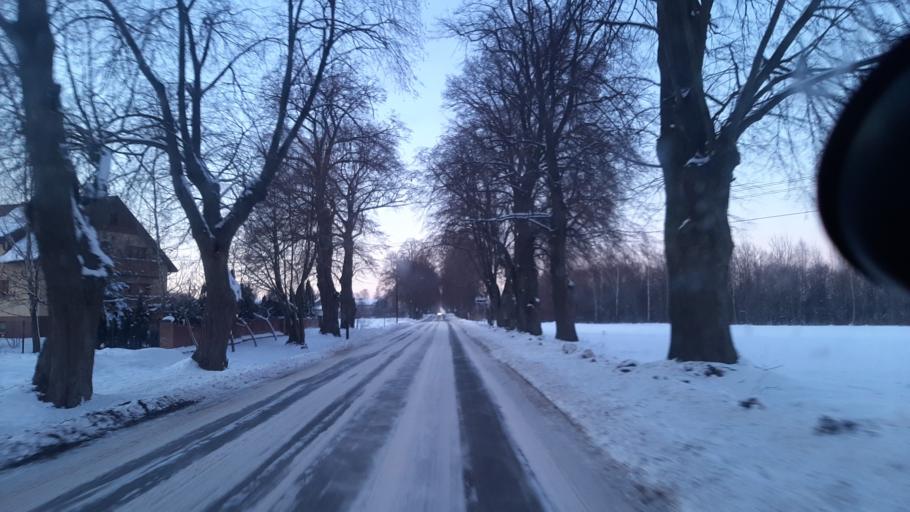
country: PL
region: Lublin Voivodeship
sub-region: Powiat lubelski
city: Lublin
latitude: 51.3296
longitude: 22.5568
